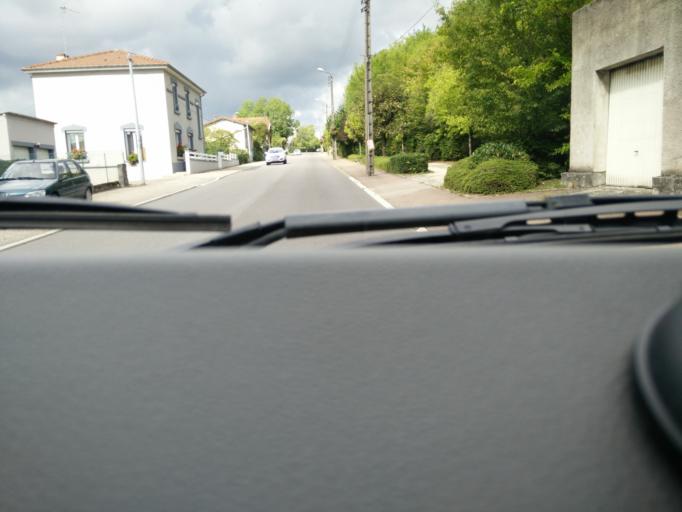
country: FR
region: Lorraine
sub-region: Departement de la Meuse
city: Belleville-sur-Meuse
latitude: 49.1776
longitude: 5.3746
